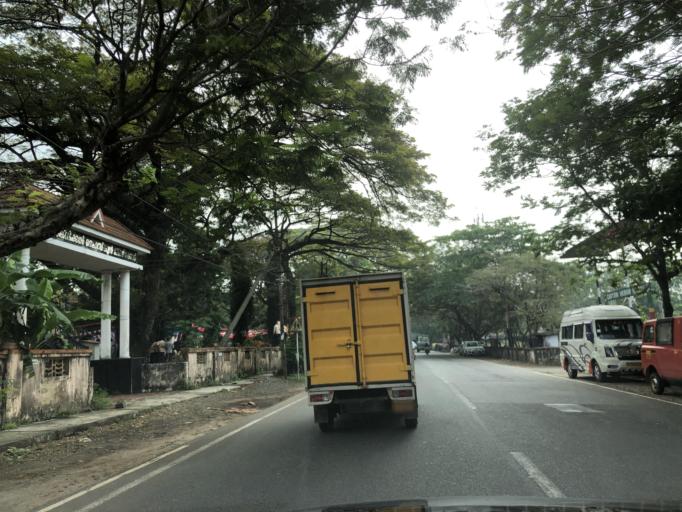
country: IN
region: Kerala
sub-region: Kozhikode
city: Kozhikode
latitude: 11.2868
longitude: 75.7676
